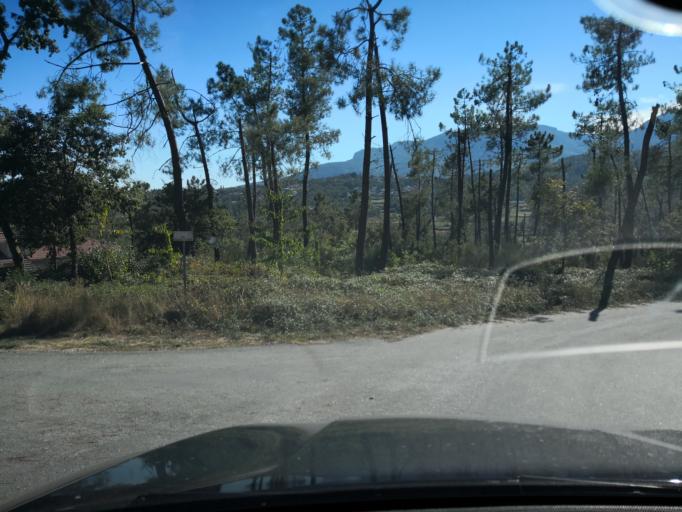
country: PT
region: Vila Real
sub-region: Santa Marta de Penaguiao
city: Santa Marta de Penaguiao
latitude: 41.2929
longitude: -7.8620
